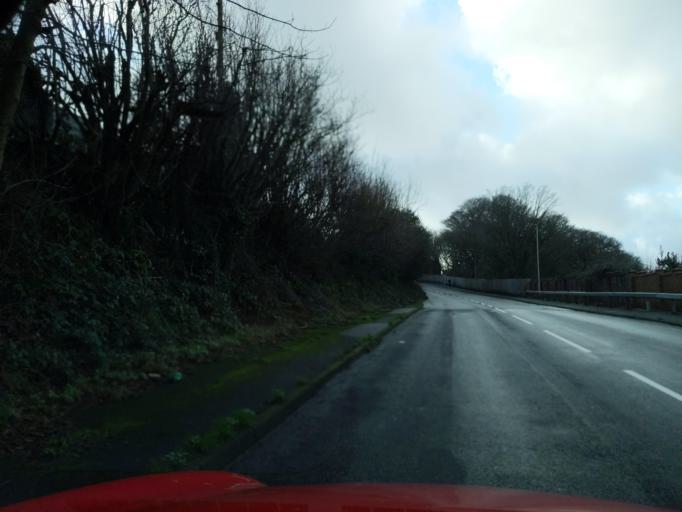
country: GB
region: England
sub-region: Plymouth
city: Plymstock
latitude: 50.3538
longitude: -4.0735
